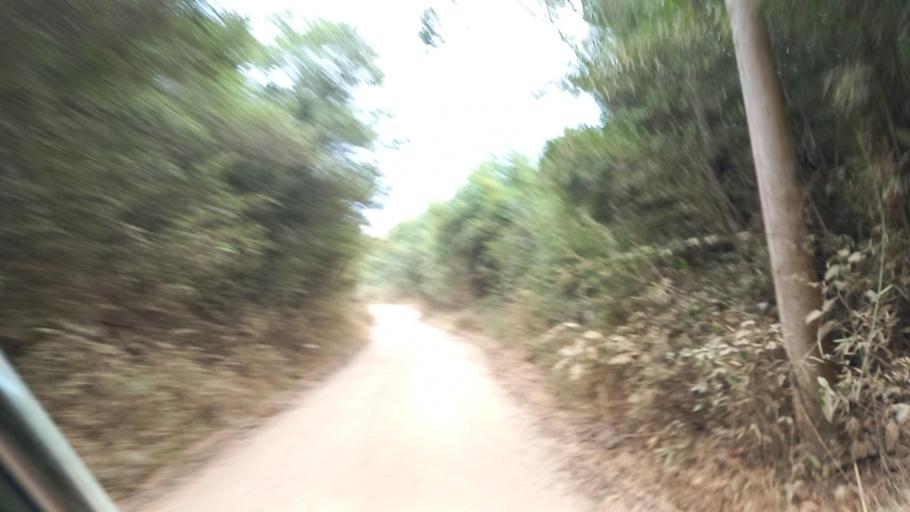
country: BR
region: Sao Paulo
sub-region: Moji-Guacu
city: Mogi-Gaucu
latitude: -22.2984
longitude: -46.8332
